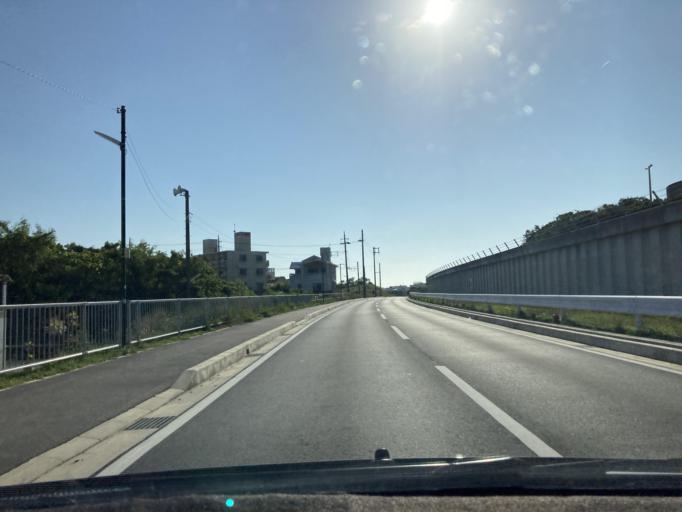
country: JP
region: Okinawa
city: Ginowan
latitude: 26.2708
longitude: 127.7644
